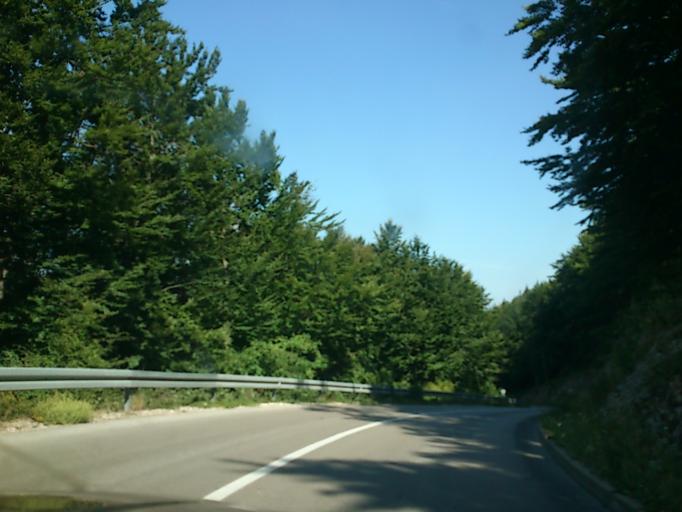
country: HR
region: Licko-Senjska
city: Otocac
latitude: 44.8464
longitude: 15.1257
